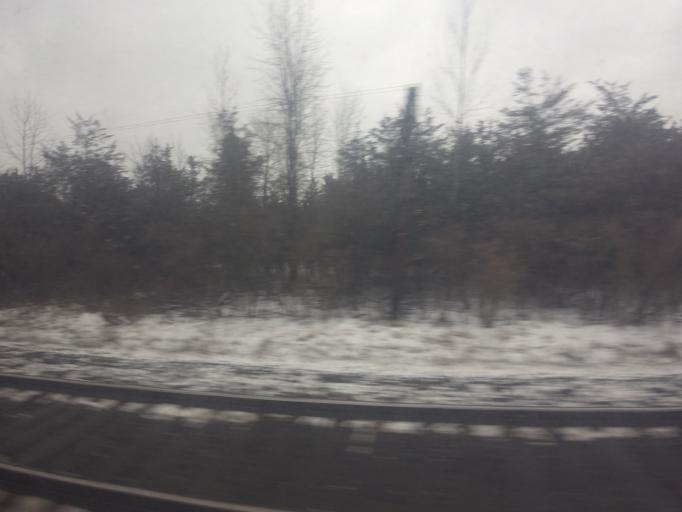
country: CA
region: Ontario
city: Quinte West
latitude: 44.1487
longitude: -77.4874
